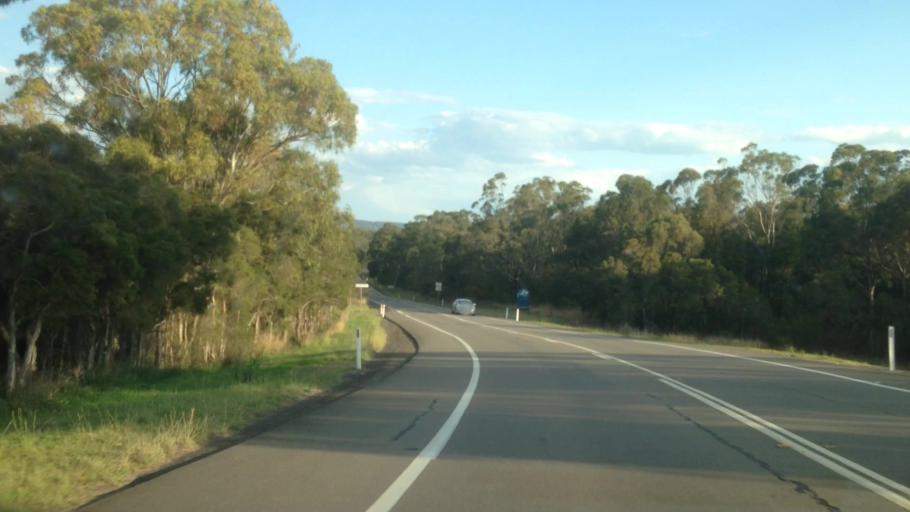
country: AU
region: New South Wales
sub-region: Cessnock
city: Kurri Kurri
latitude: -32.8344
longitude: 151.4805
